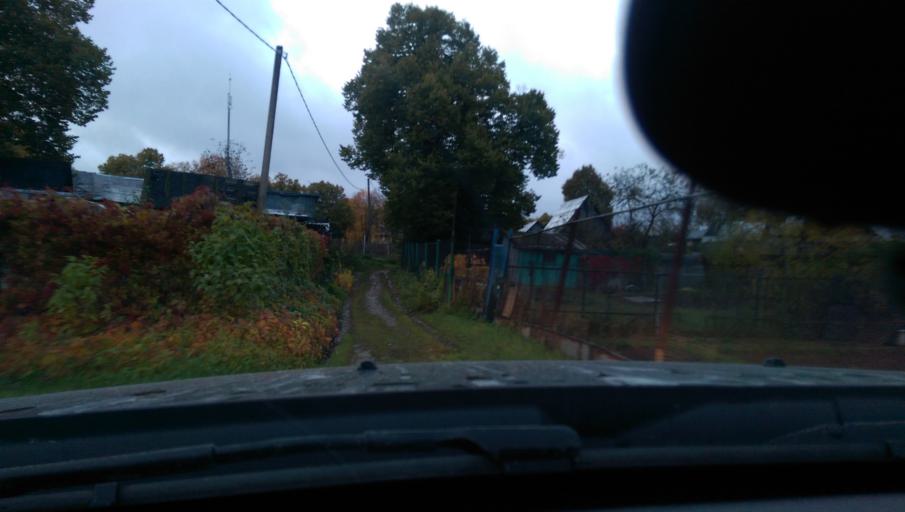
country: RU
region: Moskovskaya
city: Radumlya
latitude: 56.0906
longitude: 37.1537
